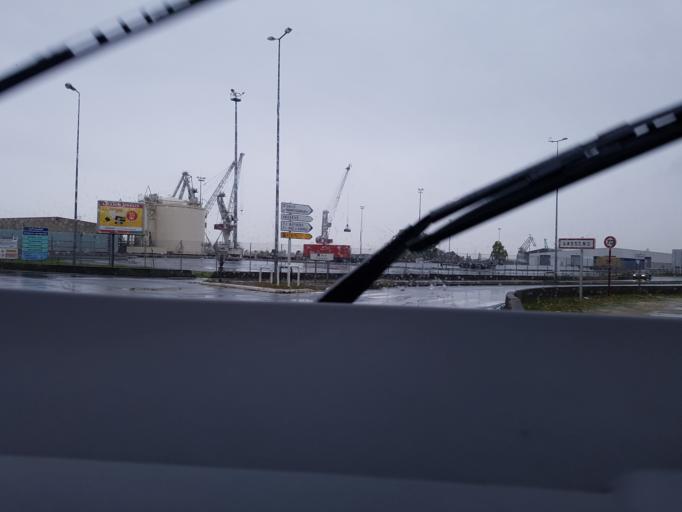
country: FR
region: Aquitaine
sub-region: Departement de la Gironde
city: Lormont
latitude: 44.8888
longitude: -0.5293
